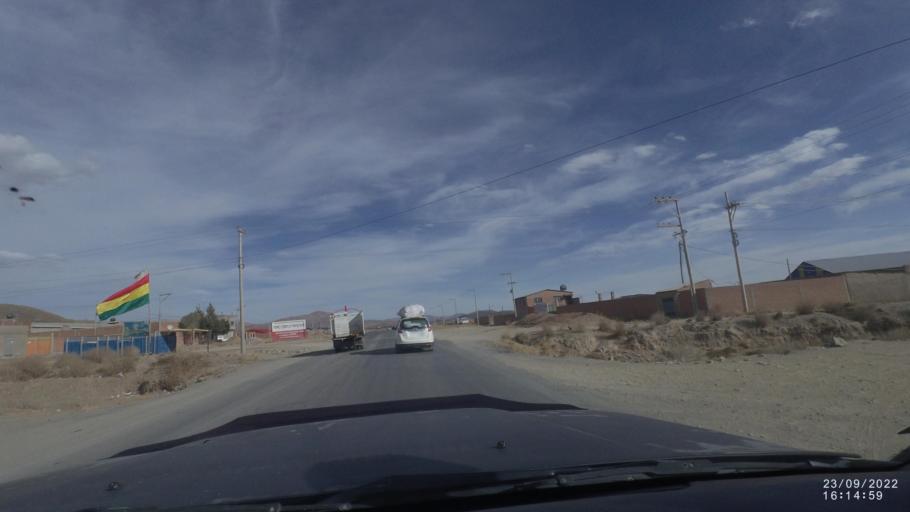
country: BO
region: Oruro
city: Oruro
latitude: -17.9967
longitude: -67.0453
